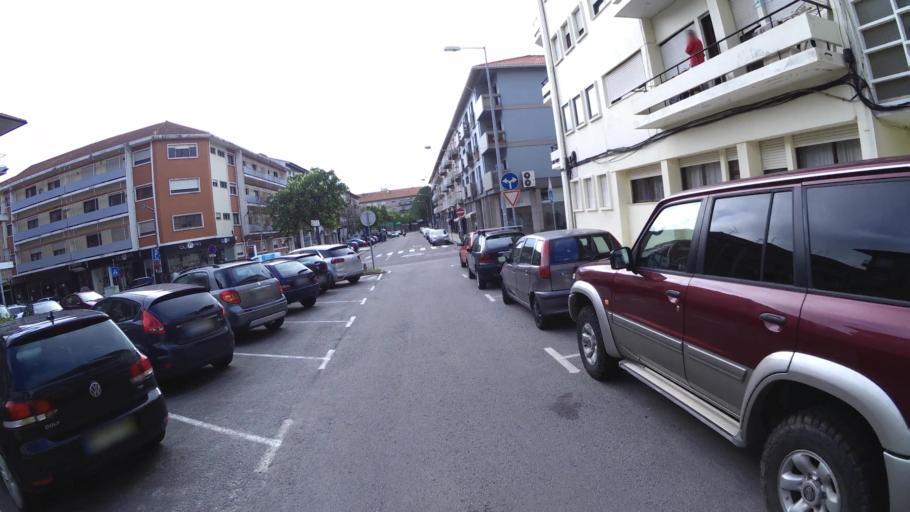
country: PT
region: Aveiro
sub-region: Aveiro
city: Aveiro
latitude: 40.6441
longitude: -8.6467
